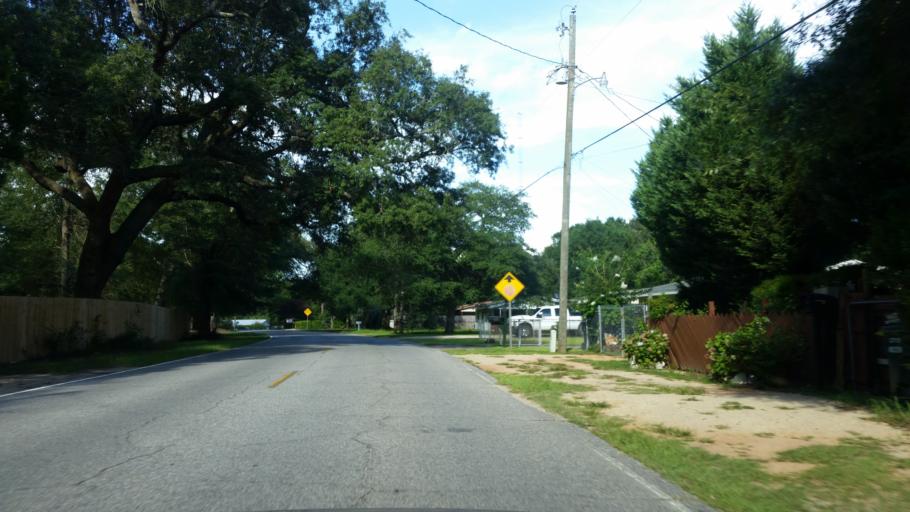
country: US
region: Florida
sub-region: Santa Rosa County
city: Milton
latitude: 30.6249
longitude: -87.0503
